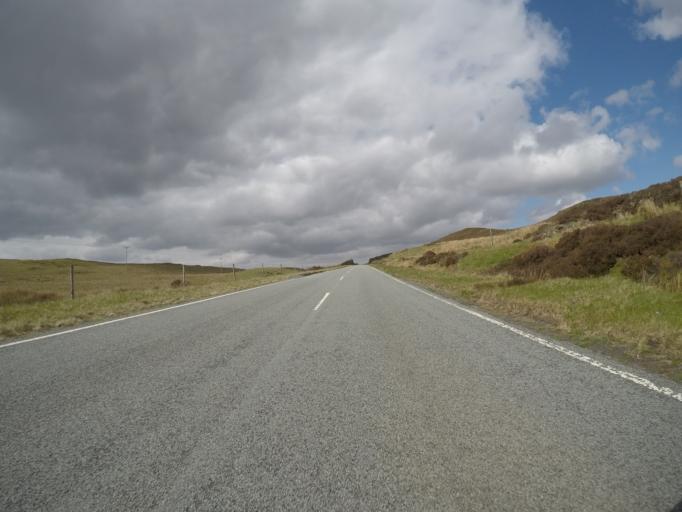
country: GB
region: Scotland
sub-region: Highland
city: Isle of Skye
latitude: 57.3090
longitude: -6.3175
